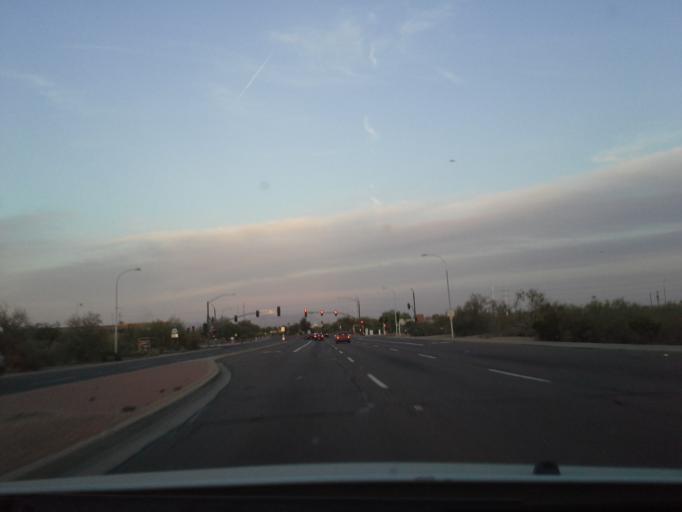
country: US
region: Arizona
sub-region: Maricopa County
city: Tempe Junction
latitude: 33.4660
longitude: -111.9454
